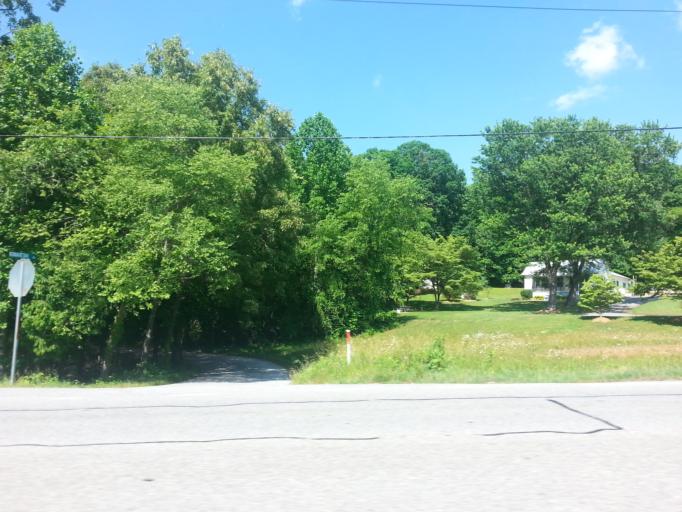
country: US
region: Georgia
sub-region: Towns County
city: Hiawassee
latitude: 34.9352
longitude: -83.7373
